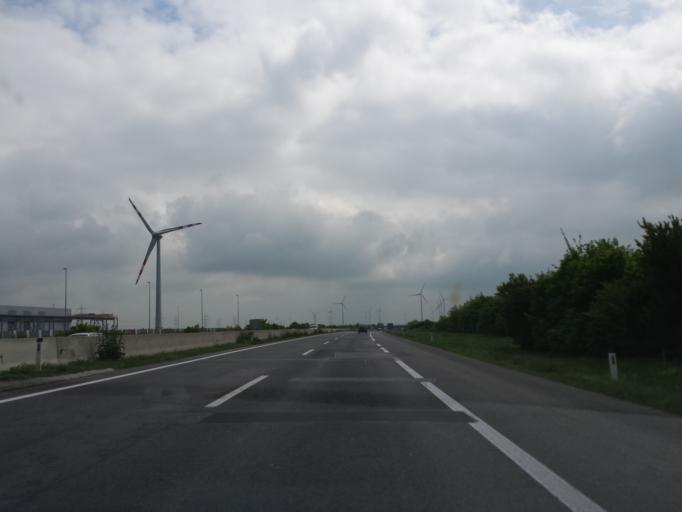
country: AT
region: Burgenland
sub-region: Politischer Bezirk Neusiedl am See
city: Zurndorf
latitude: 47.9353
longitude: 16.9871
